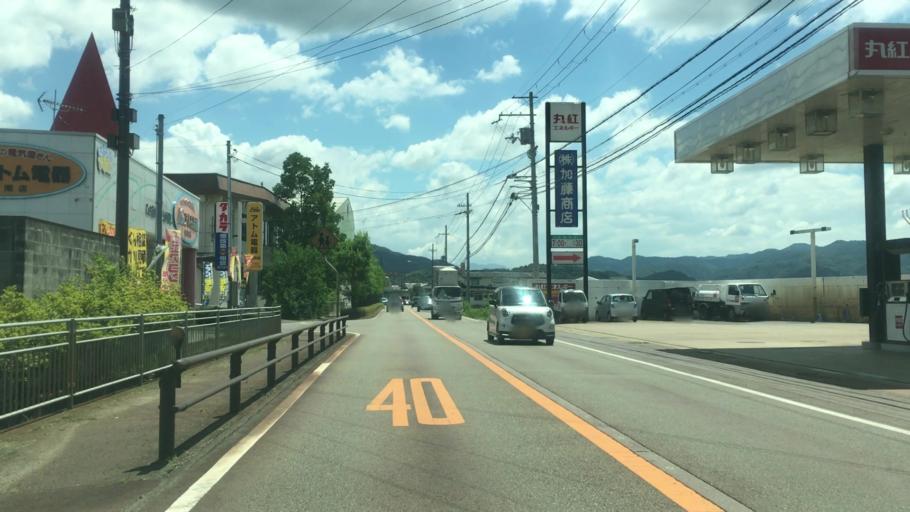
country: JP
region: Hyogo
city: Toyooka
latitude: 35.4924
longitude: 134.8005
